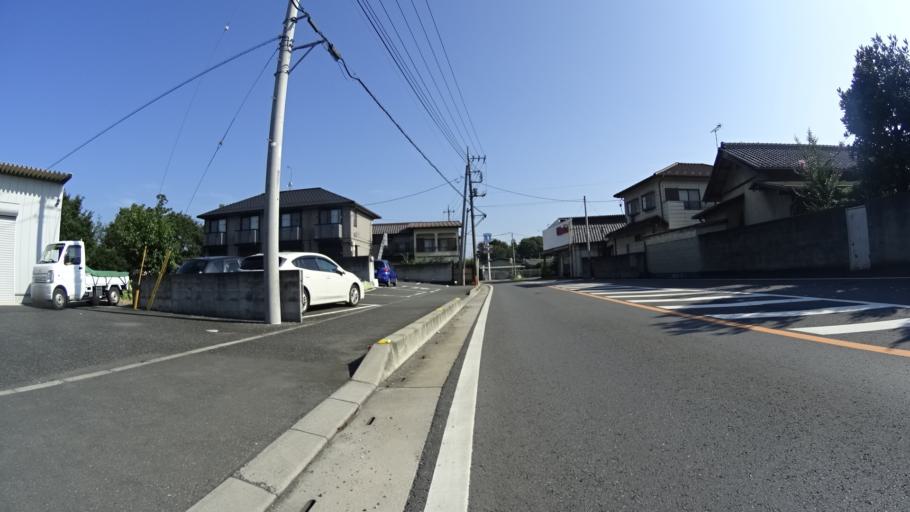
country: JP
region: Saitama
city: Chichibu
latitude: 36.0083
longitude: 139.0873
